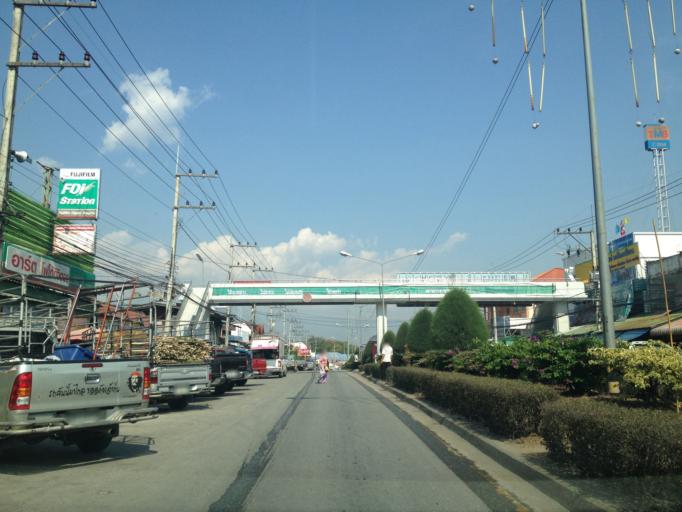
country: TH
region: Chiang Mai
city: Hot
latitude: 18.1944
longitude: 98.6116
